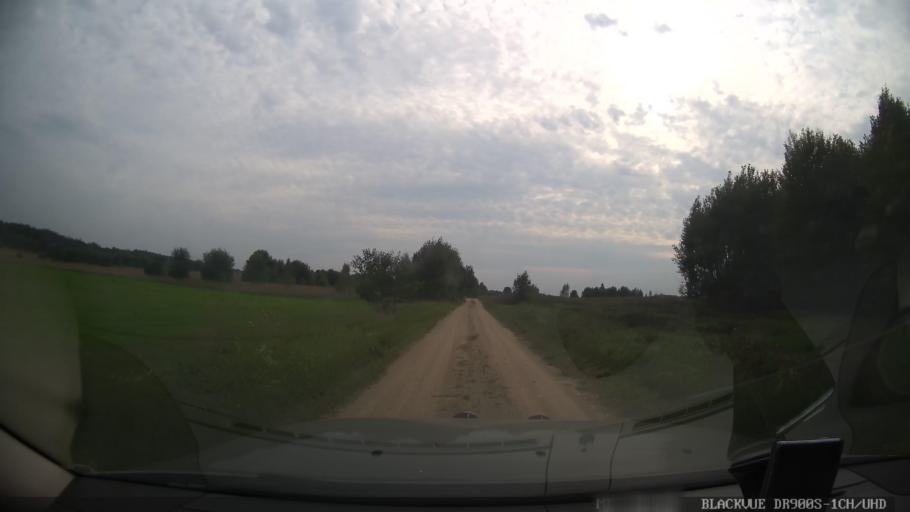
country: BY
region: Grodnenskaya
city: Ashmyany
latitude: 54.5357
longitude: 25.6741
